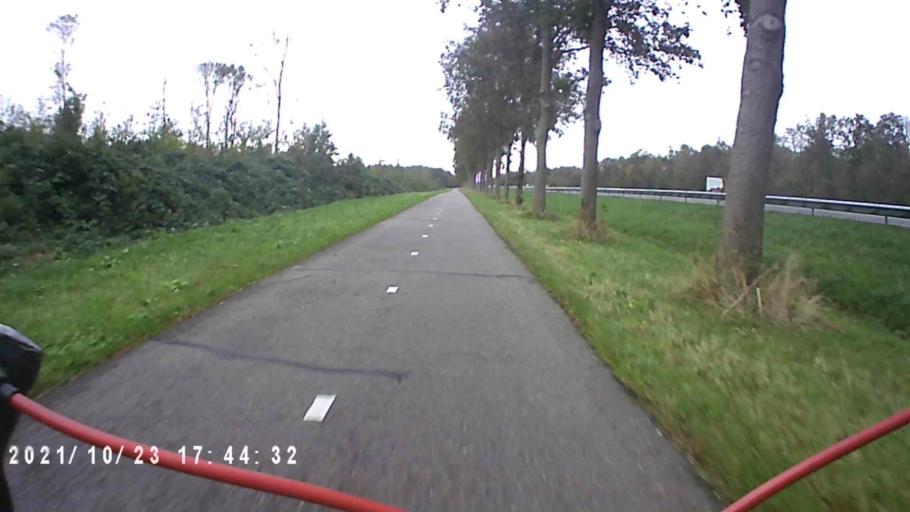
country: NL
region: North Holland
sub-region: Gemeente Hollands Kroon
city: Den Oever
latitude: 52.9001
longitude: 5.0274
